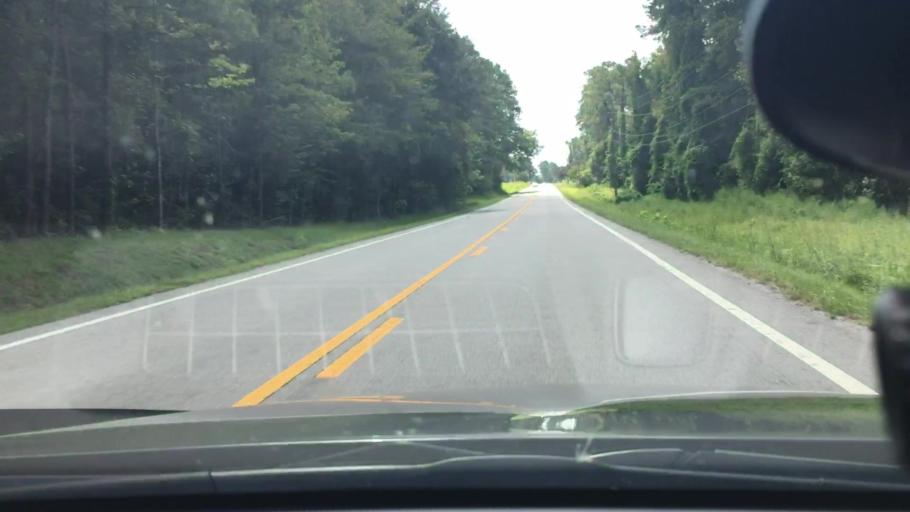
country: US
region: North Carolina
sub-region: Pitt County
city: Farmville
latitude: 35.6867
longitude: -77.4942
